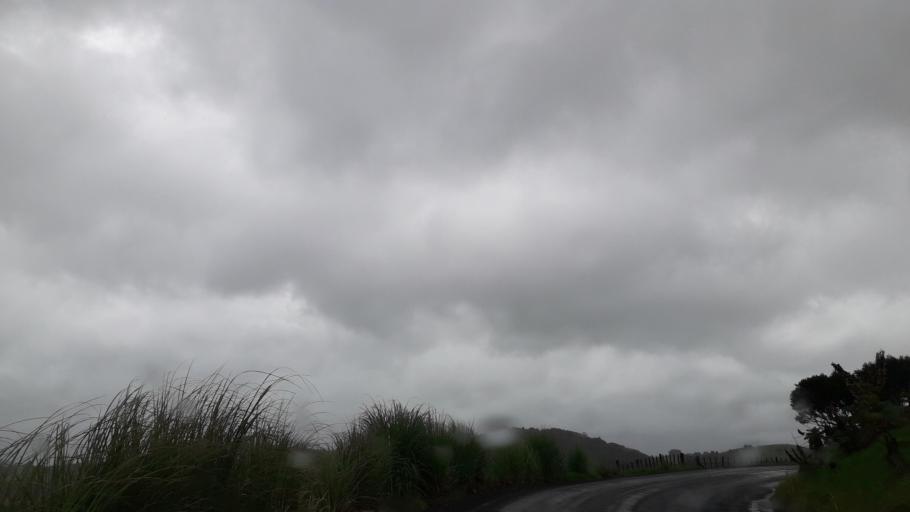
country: NZ
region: Northland
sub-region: Far North District
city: Kaitaia
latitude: -35.4079
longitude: 173.3635
